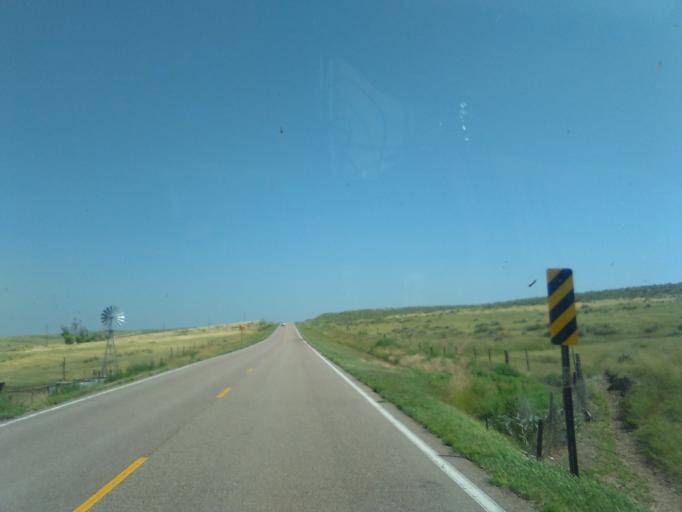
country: US
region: Nebraska
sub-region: Dundy County
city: Benkelman
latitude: 39.9345
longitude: -101.5412
